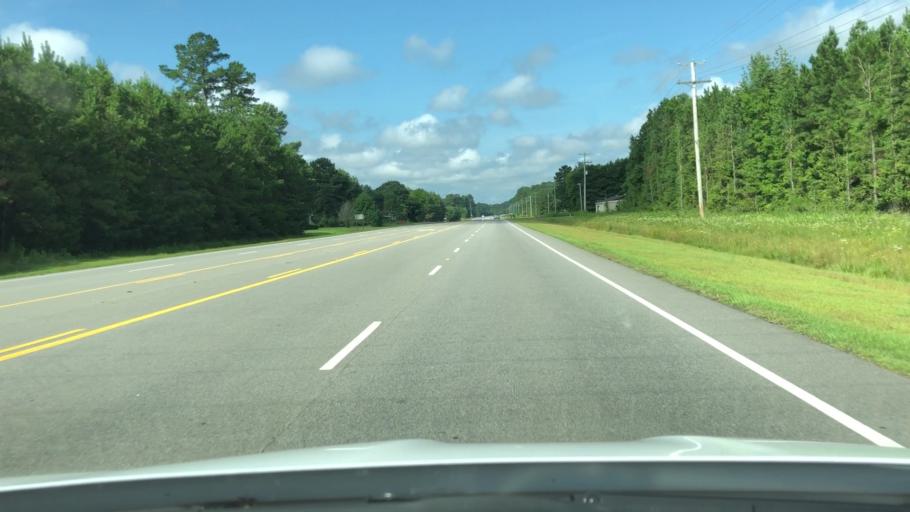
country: US
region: North Carolina
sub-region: Bertie County
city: Windsor
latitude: 36.0230
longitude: -76.8181
